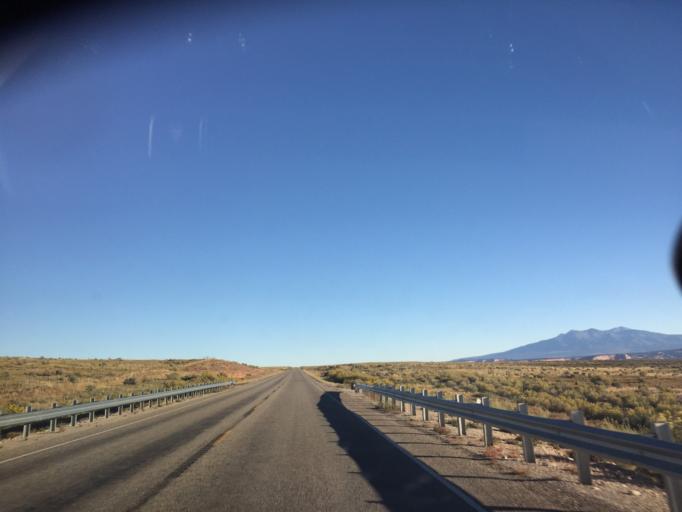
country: US
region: Utah
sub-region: San Juan County
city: Monticello
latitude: 38.1173
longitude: -109.3658
